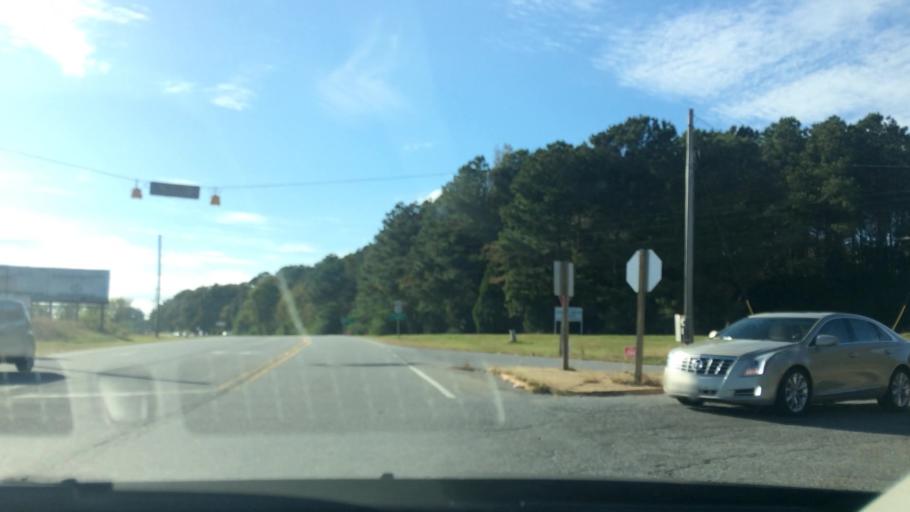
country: US
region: North Carolina
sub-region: Greene County
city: Snow Hill
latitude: 35.4594
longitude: -77.7040
